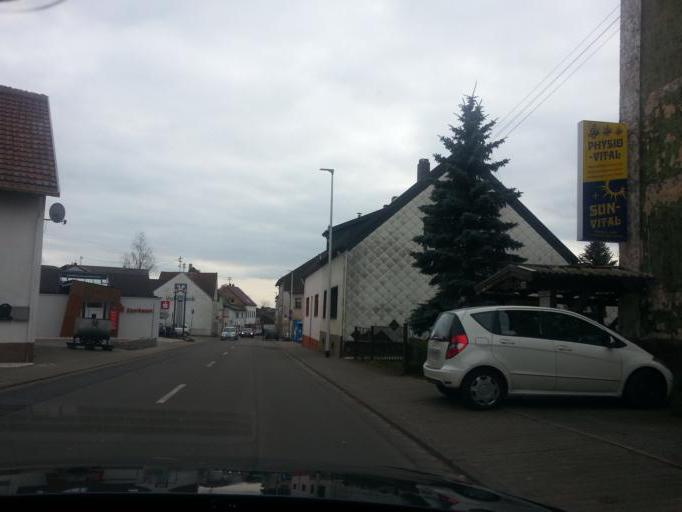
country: DE
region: Saarland
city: Bexbach
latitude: 49.3787
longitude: 7.2538
